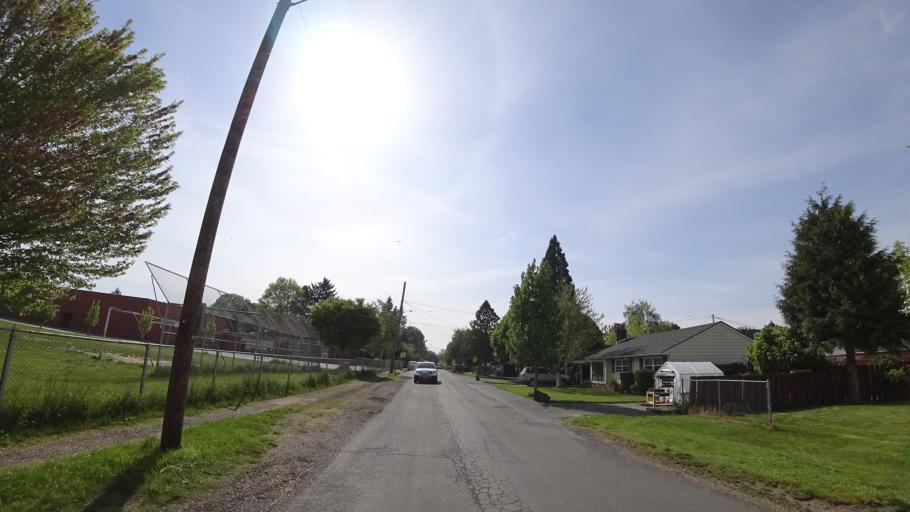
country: US
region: Oregon
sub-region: Clackamas County
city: Milwaukie
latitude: 45.4747
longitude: -122.6169
